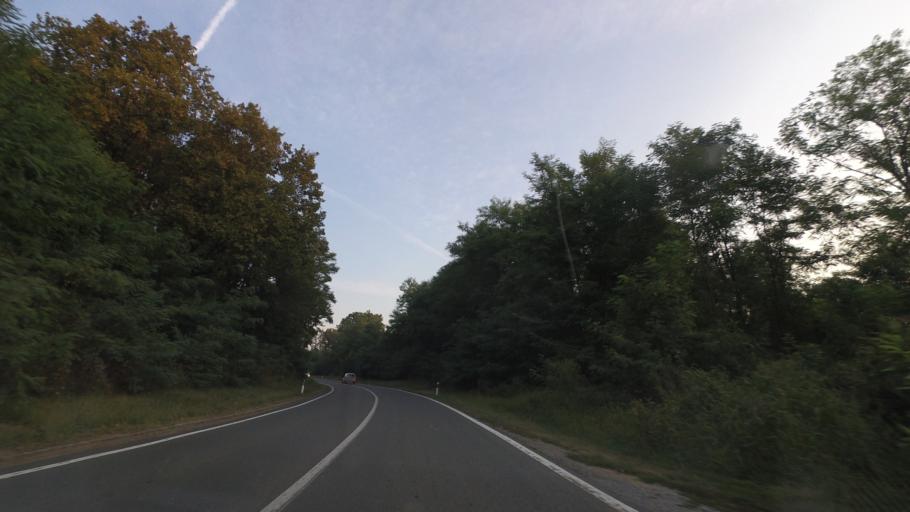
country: HR
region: Brodsko-Posavska
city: Nova Gradiska
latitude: 45.2655
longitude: 17.4102
